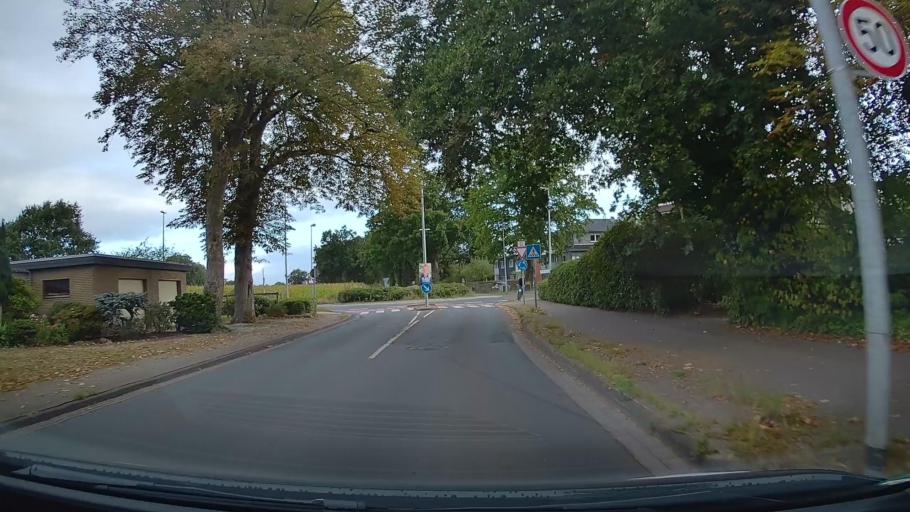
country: DE
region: Lower Saxony
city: Oldenburg
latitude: 53.1399
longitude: 8.1461
